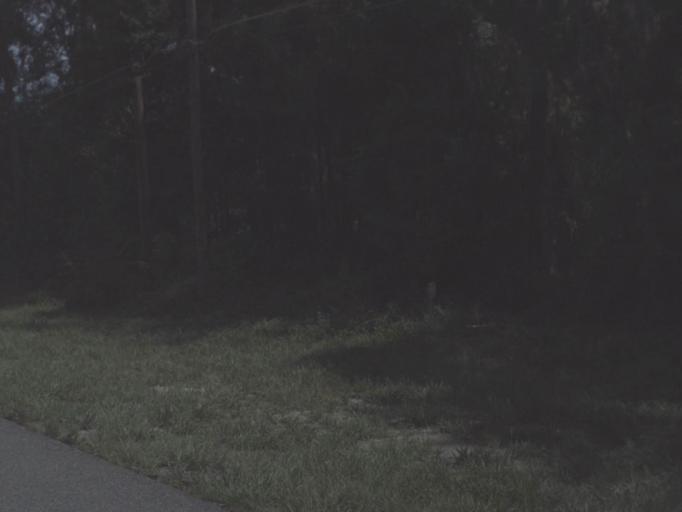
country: US
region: Florida
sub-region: Hamilton County
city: Jasper
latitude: 30.5298
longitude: -82.9684
